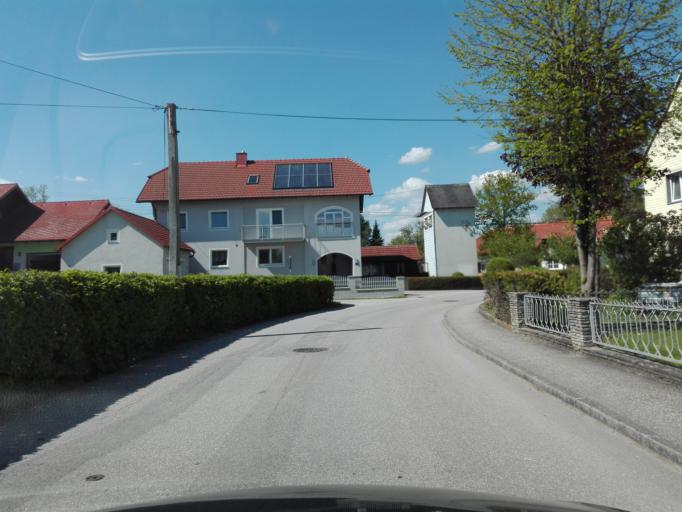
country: AT
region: Upper Austria
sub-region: Politischer Bezirk Grieskirchen
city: Bad Schallerbach
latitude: 48.3176
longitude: 13.9006
